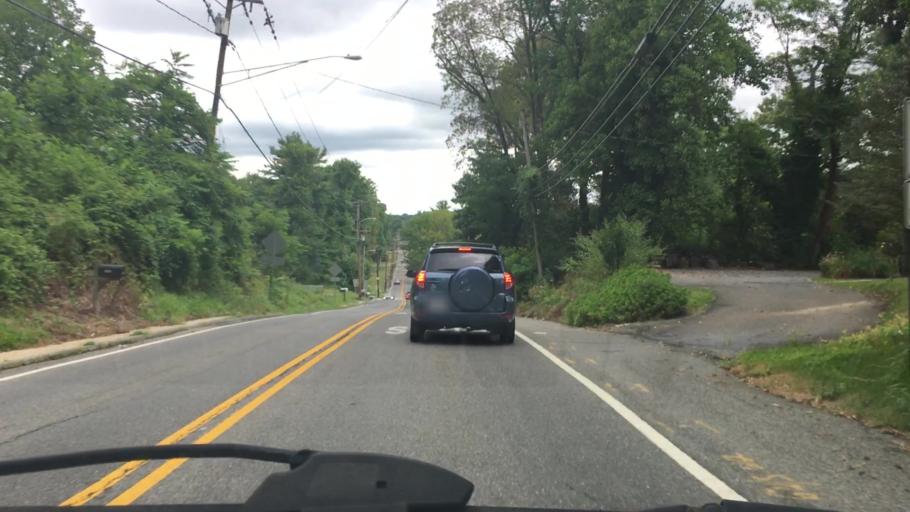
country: US
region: Maryland
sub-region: Prince George's County
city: Glenn Dale
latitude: 38.9805
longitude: -76.7715
